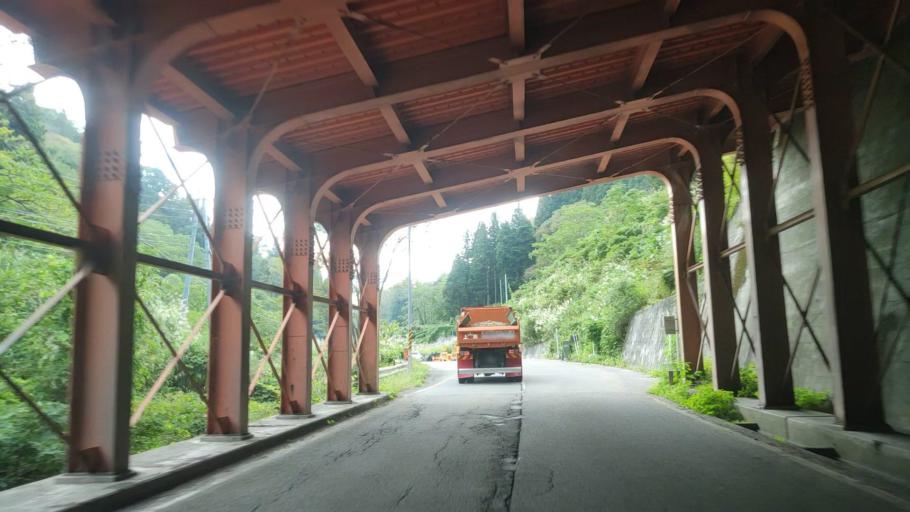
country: JP
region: Nagano
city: Iiyama
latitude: 36.9021
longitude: 138.3177
